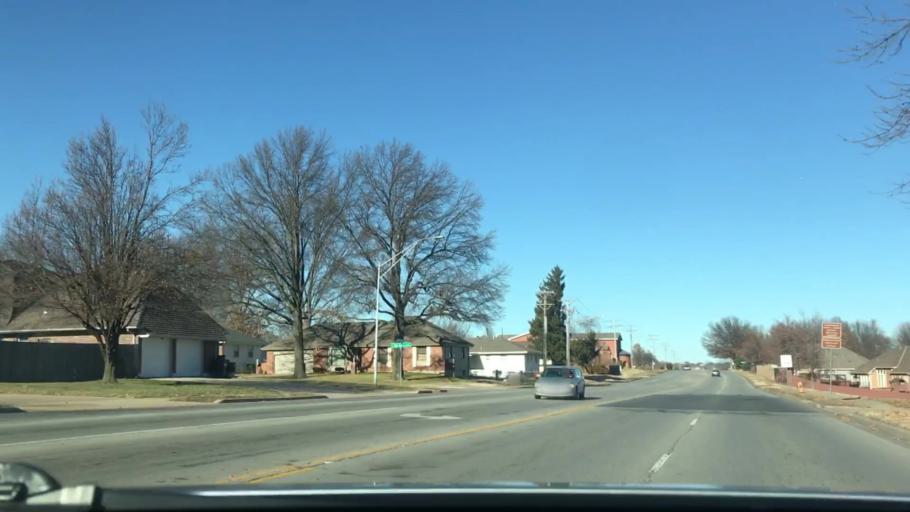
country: US
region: Missouri
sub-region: Jackson County
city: Independence
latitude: 39.0492
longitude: -94.3872
